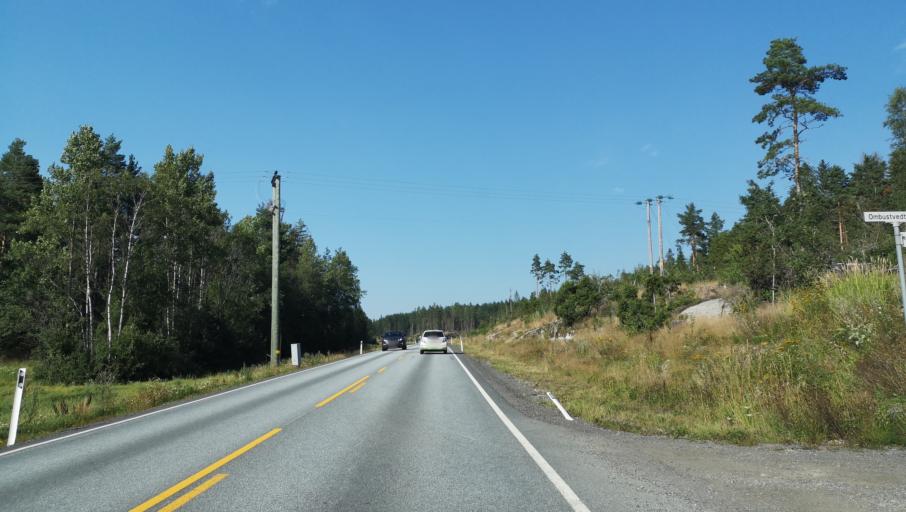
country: NO
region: Ostfold
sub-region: Valer
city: Kirkebygda
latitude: 59.5148
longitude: 10.8404
